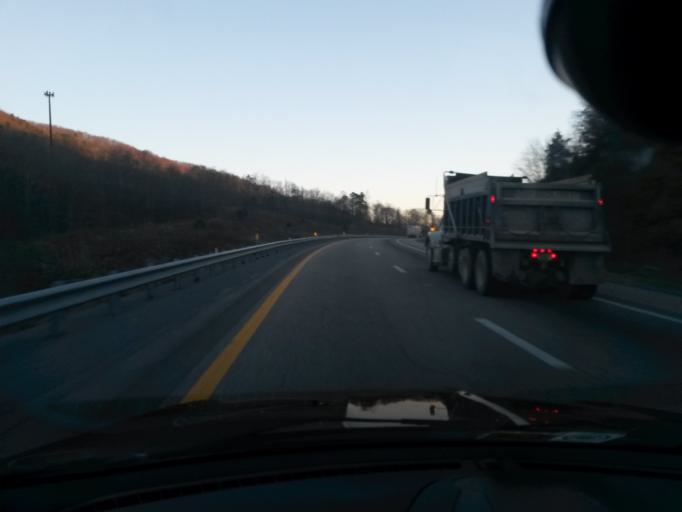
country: US
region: Virginia
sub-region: City of Lexington
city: Lexington
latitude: 37.8684
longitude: -79.6237
